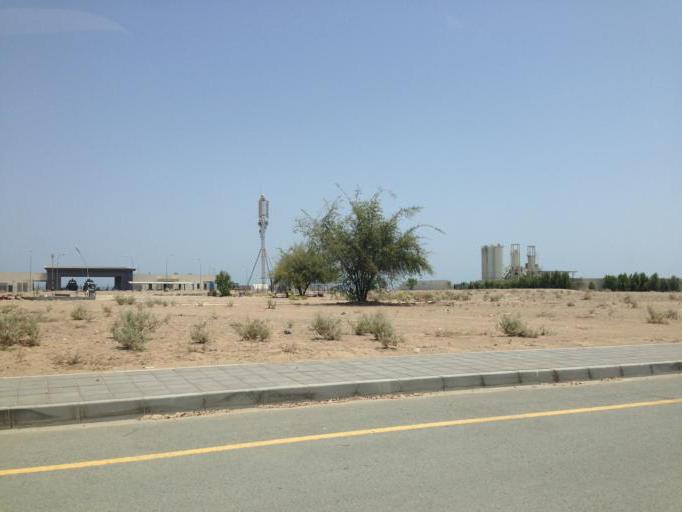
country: OM
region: Muhafazat Masqat
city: Bawshar
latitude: 23.6061
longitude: 58.3228
